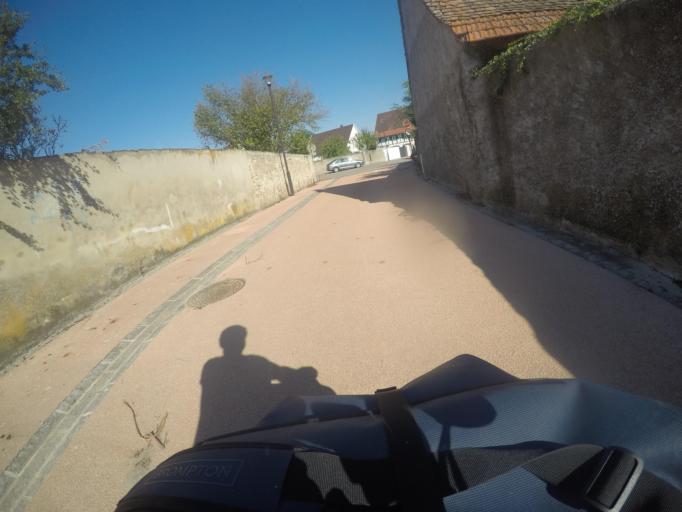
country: FR
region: Alsace
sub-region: Departement du Haut-Rhin
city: Ottmarsheim
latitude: 47.7886
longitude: 7.5075
